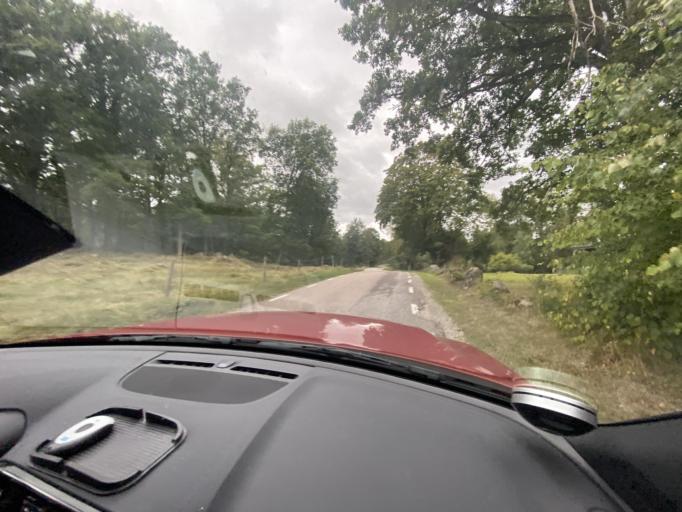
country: SE
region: Kronoberg
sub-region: Markaryds Kommun
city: Markaryd
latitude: 56.4986
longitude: 13.5373
